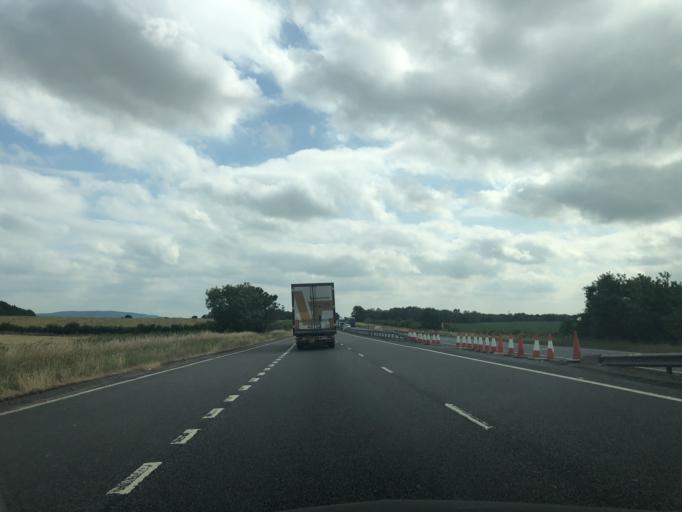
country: GB
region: England
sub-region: Stockton-on-Tees
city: Yarm
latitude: 54.4516
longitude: -1.3222
